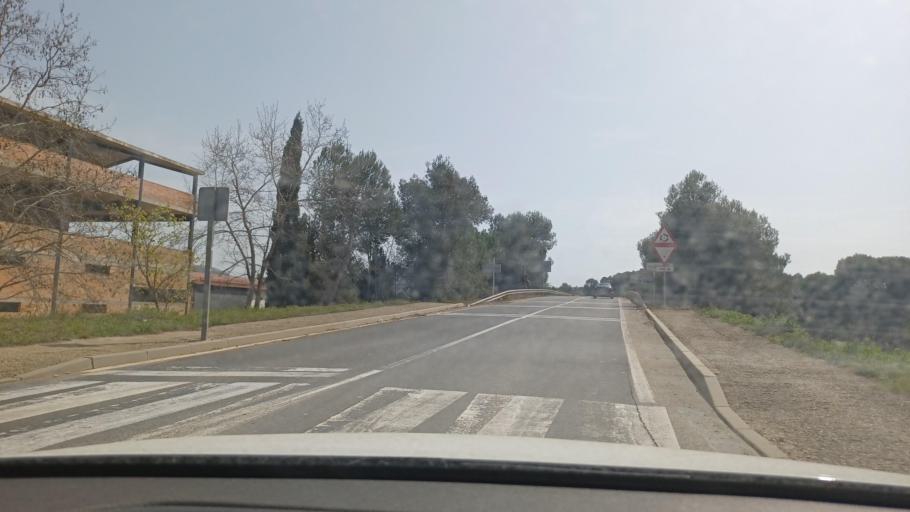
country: ES
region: Catalonia
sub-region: Provincia de Tarragona
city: Ulldecona
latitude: 40.5924
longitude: 0.4436
